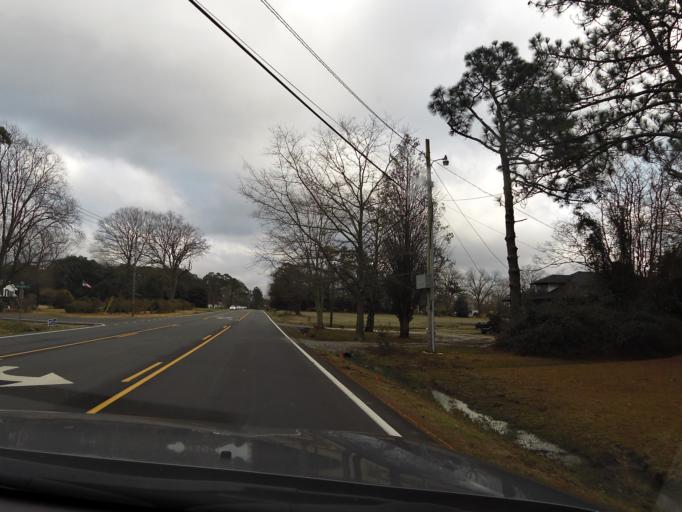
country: US
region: North Carolina
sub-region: Nash County
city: Rocky Mount
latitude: 35.9194
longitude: -77.7695
